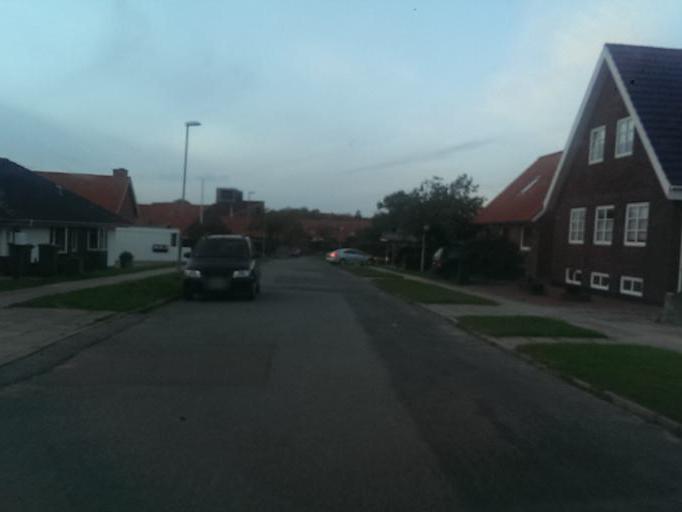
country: DK
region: South Denmark
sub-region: Esbjerg Kommune
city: Esbjerg
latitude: 55.4651
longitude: 8.4739
